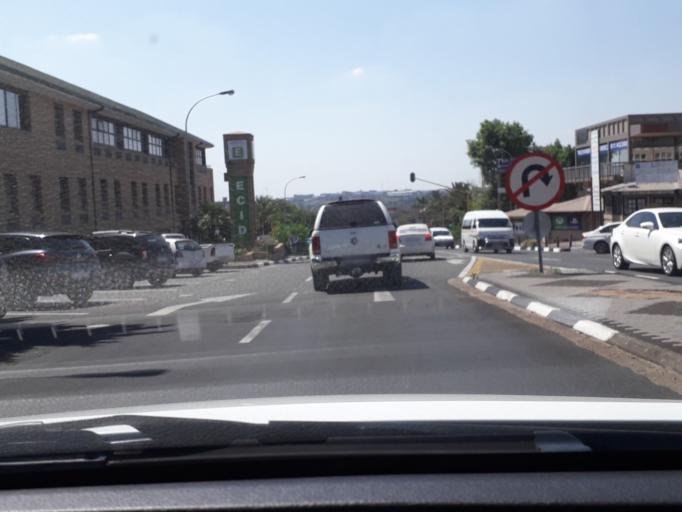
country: ZA
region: Gauteng
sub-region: City of Johannesburg Metropolitan Municipality
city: Modderfontein
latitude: -26.1417
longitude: 28.1532
